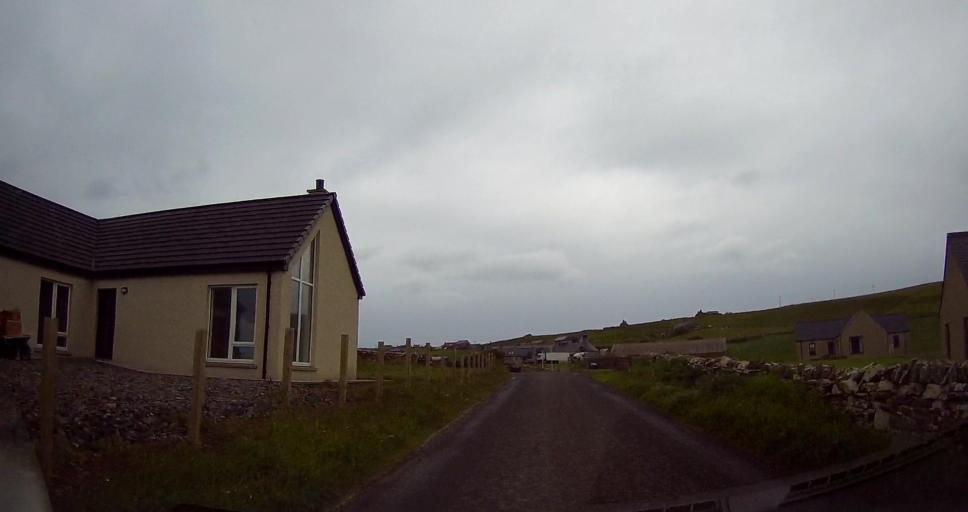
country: GB
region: Scotland
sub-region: Orkney Islands
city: Stromness
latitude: 59.0691
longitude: -3.3050
